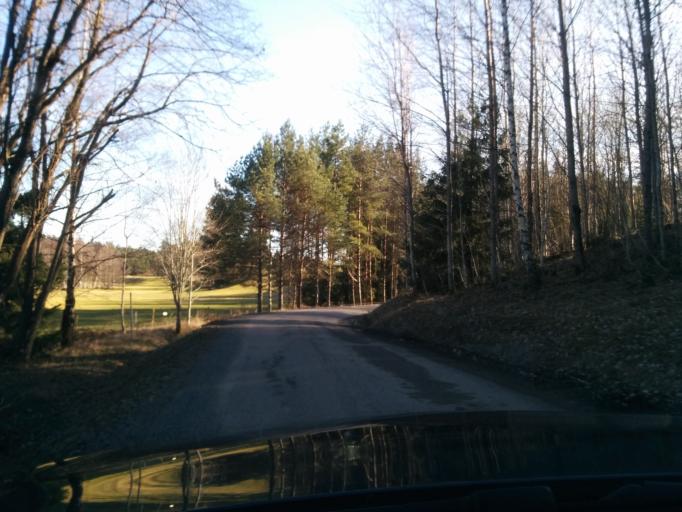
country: SE
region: Stockholm
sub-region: Vallentuna Kommun
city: Vallentuna
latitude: 59.5059
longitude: 18.0087
